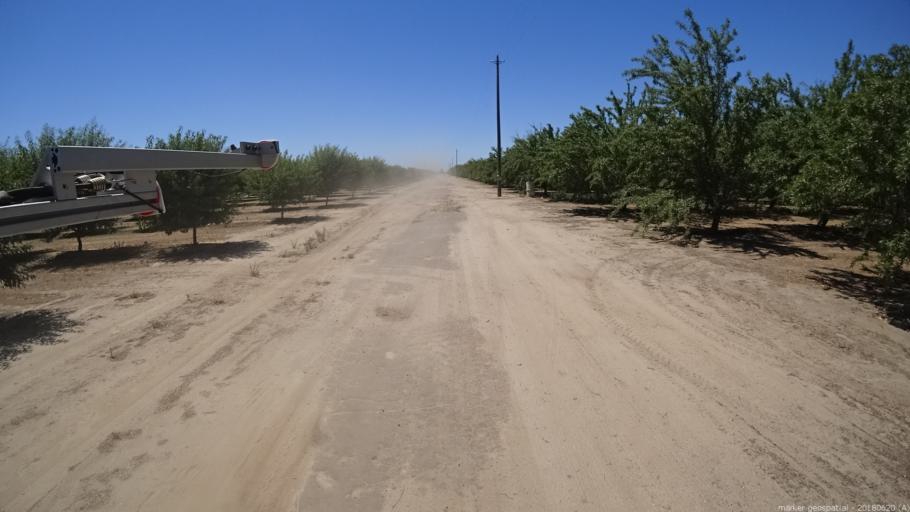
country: US
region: California
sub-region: Fresno County
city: Biola
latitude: 36.8461
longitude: -119.9741
